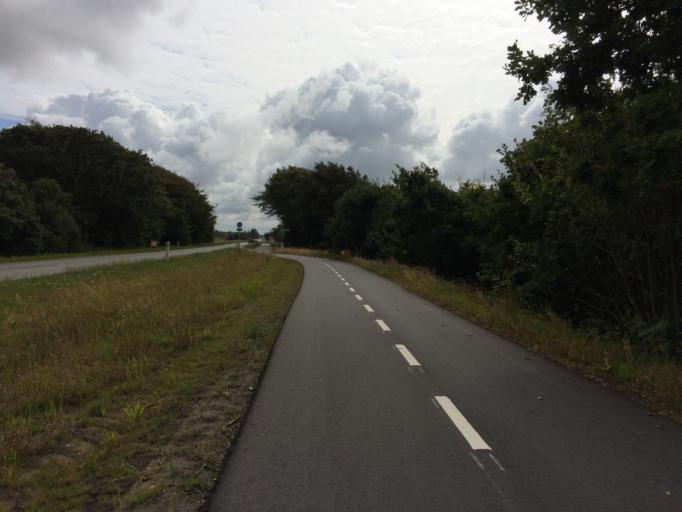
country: DK
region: Central Jutland
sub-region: Holstebro Kommune
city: Ulfborg
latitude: 56.3147
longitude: 8.3386
